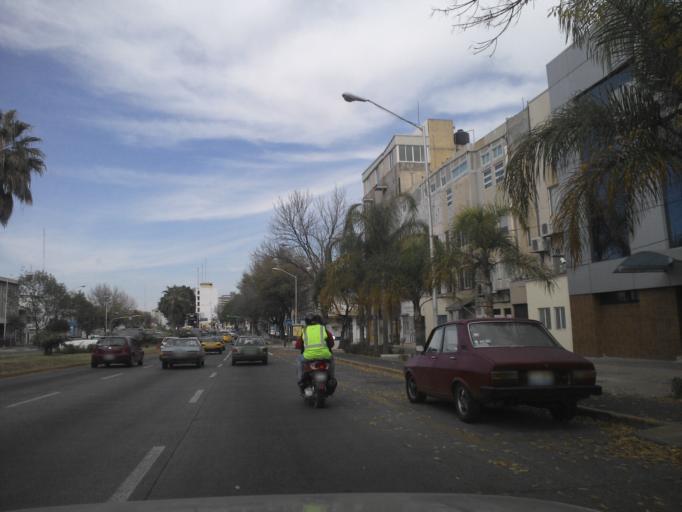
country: MX
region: Jalisco
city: Guadalajara
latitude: 20.6675
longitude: -103.3551
